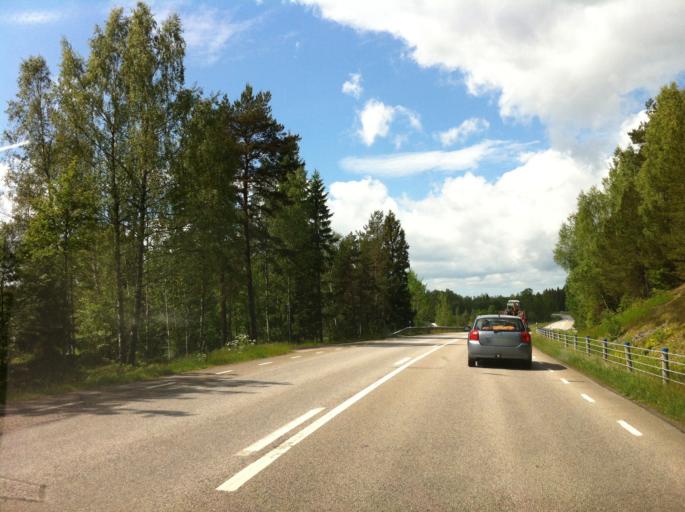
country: SE
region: Vaermland
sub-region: Saffle Kommun
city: Saeffle
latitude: 59.1526
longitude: 12.9710
